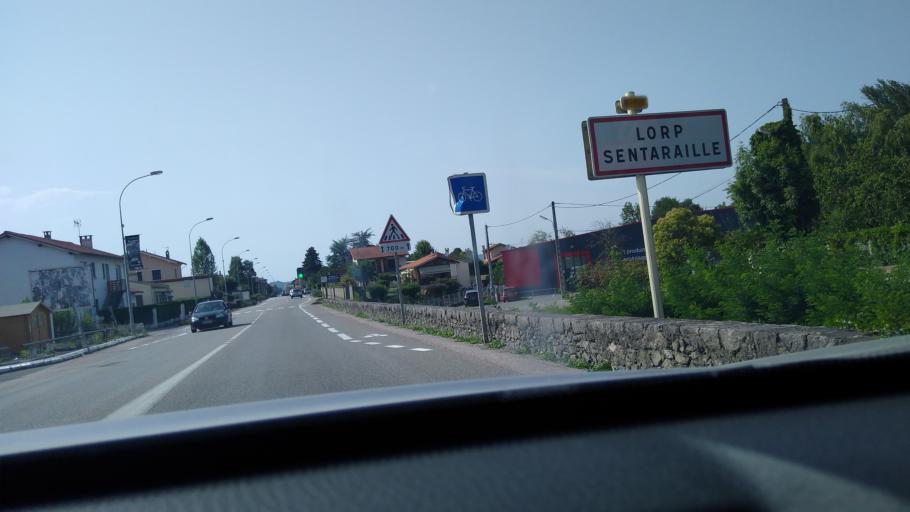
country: FR
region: Midi-Pyrenees
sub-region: Departement de l'Ariege
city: Saint-Lizier
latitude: 43.0063
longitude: 1.1249
